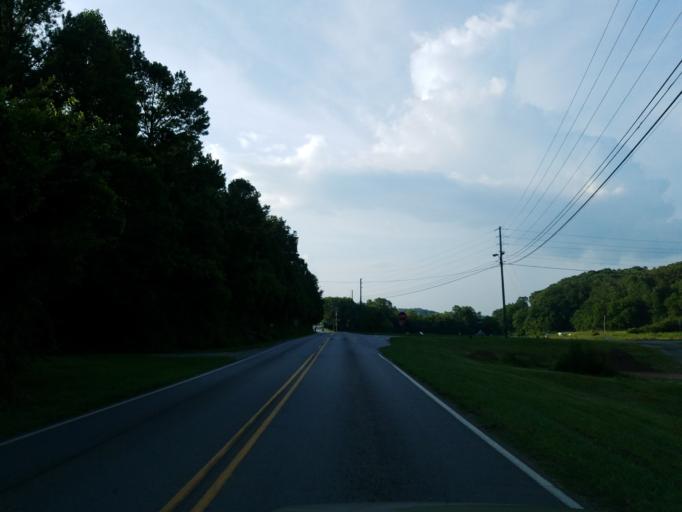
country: US
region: Georgia
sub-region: Gilmer County
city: Ellijay
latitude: 34.6599
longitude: -84.5001
